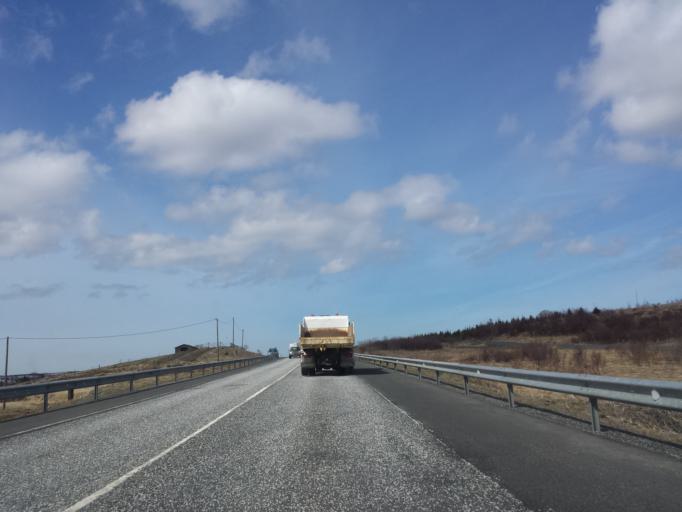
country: IS
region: Capital Region
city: Mosfellsbaer
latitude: 64.0979
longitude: -21.7444
